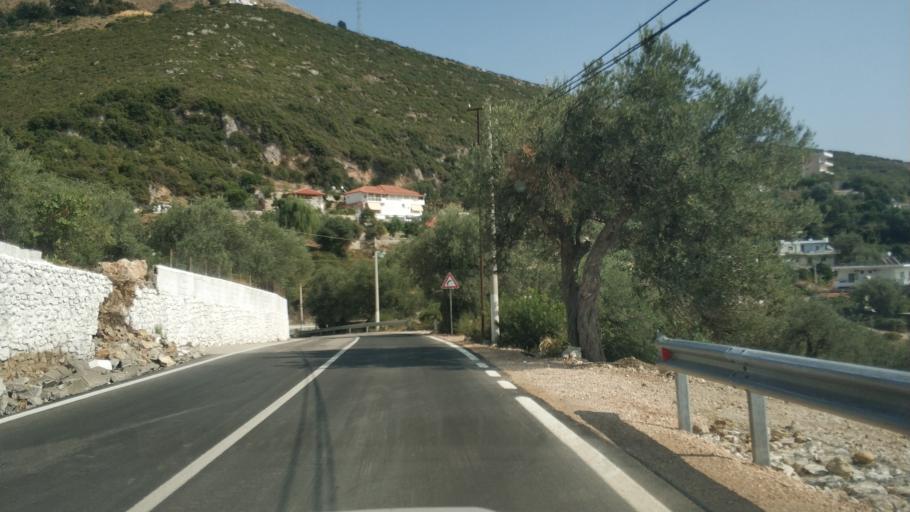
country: AL
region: Vlore
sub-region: Rrethi i Sarandes
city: Lukove
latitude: 40.0215
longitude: 19.8901
